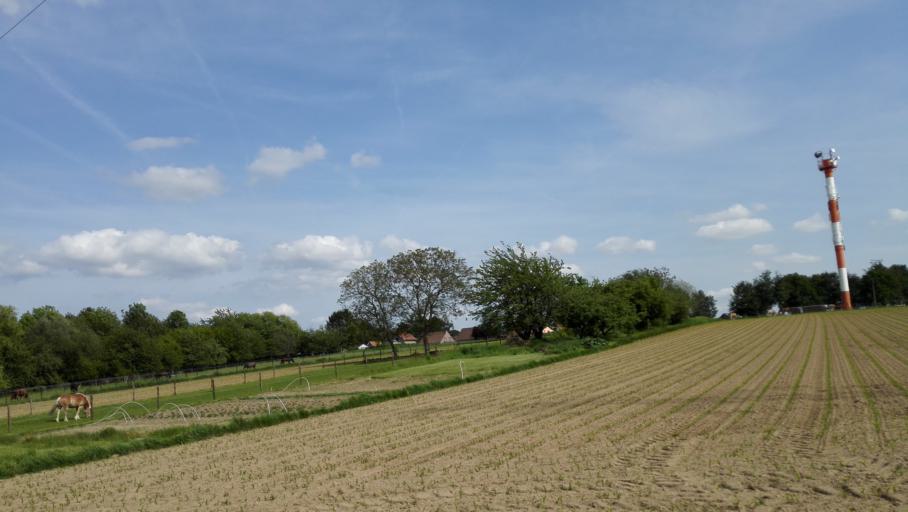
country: BE
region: Flanders
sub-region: Provincie Vlaams-Brabant
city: Bierbeek
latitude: 50.8739
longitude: 4.7552
